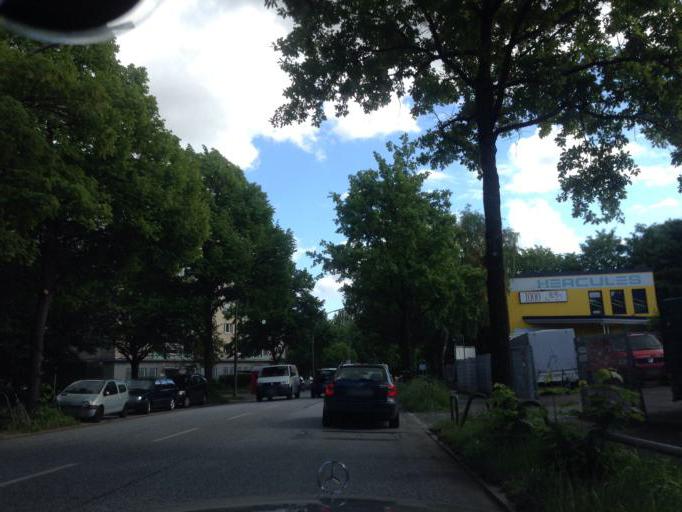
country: DE
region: Hamburg
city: Marienthal
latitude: 53.5779
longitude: 10.0583
